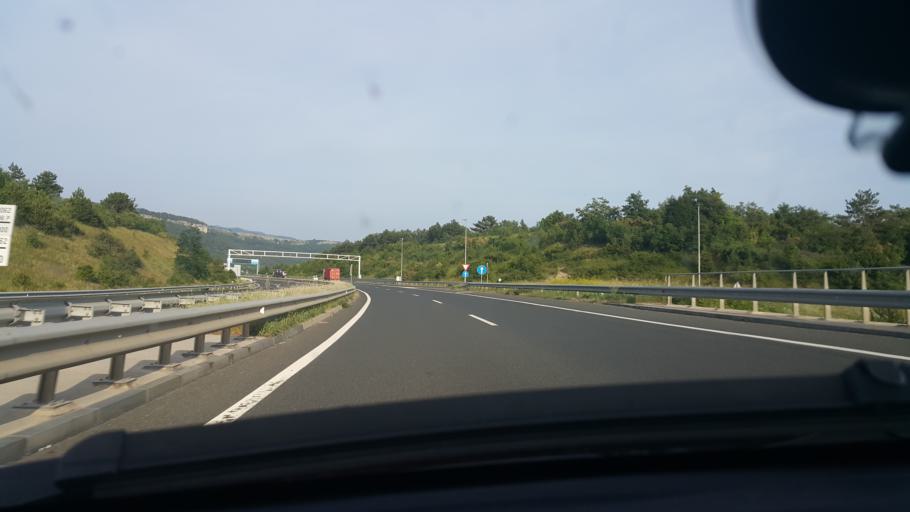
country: SI
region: Koper-Capodistria
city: Sv. Anton
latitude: 45.5534
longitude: 13.8567
